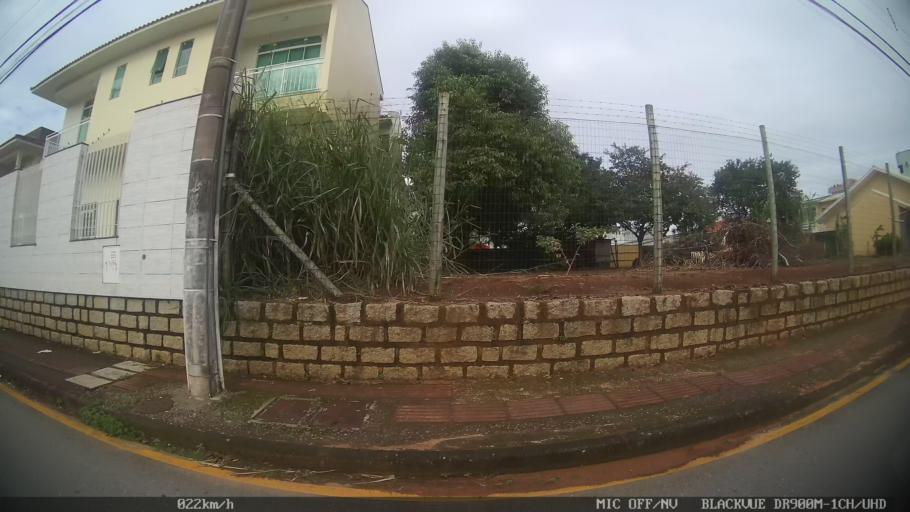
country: BR
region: Santa Catarina
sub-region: Sao Jose
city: Campinas
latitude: -27.5690
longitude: -48.6195
